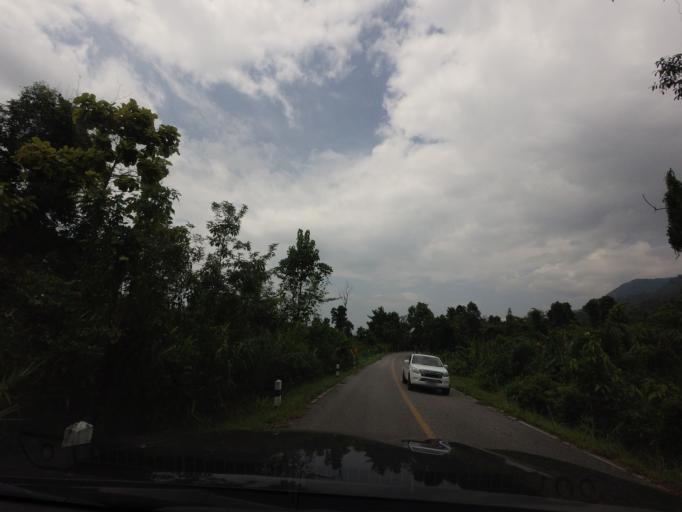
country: TH
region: Uttaradit
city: Nam Pat
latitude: 17.7341
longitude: 100.9466
